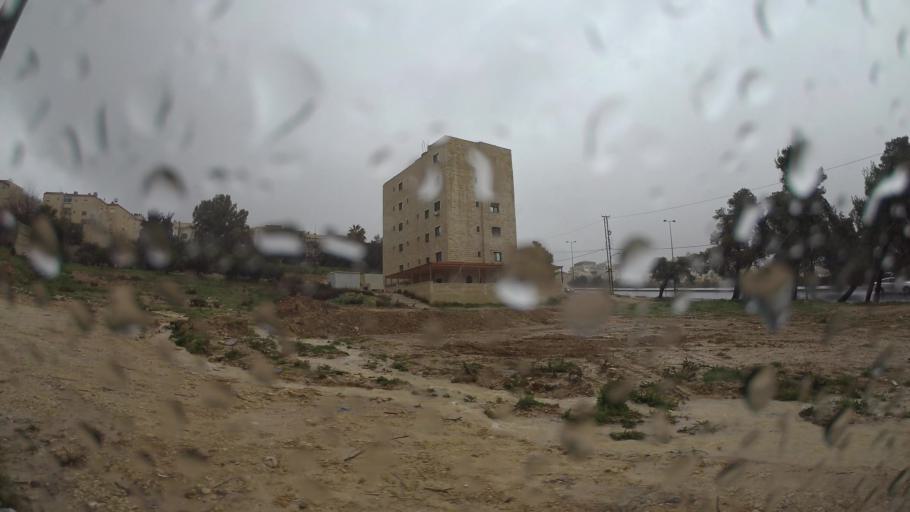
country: JO
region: Amman
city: Al Jubayhah
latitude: 32.0303
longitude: 35.8861
